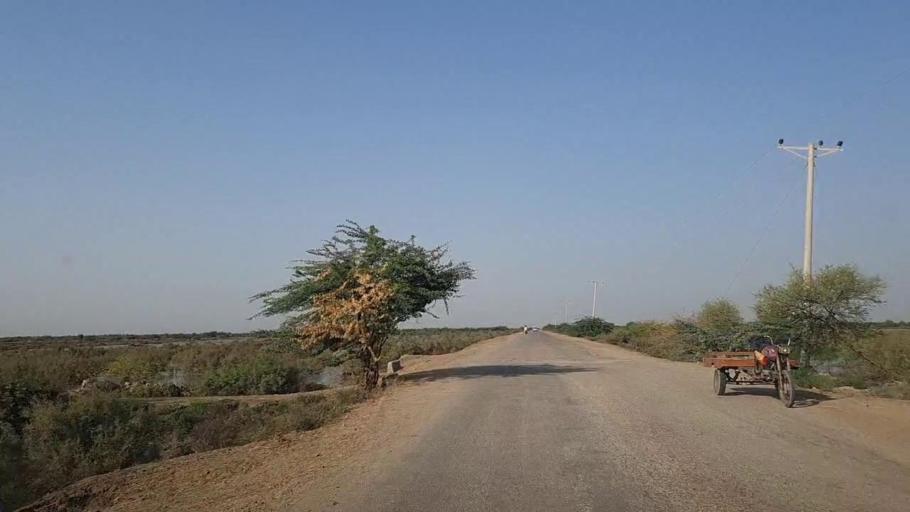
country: PK
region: Sindh
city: Mirpur Batoro
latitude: 24.6019
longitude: 68.4010
